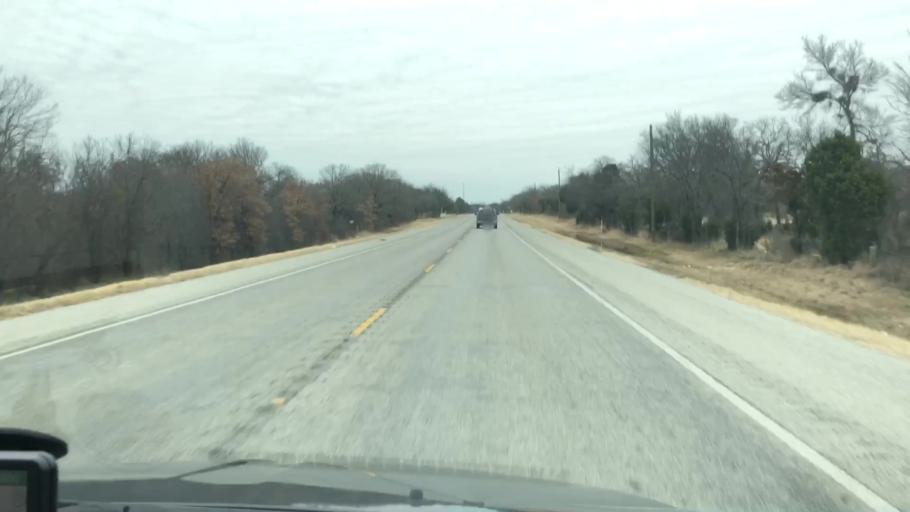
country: US
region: Texas
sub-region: Palo Pinto County
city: Mineral Wells
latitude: 32.8951
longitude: -98.0860
